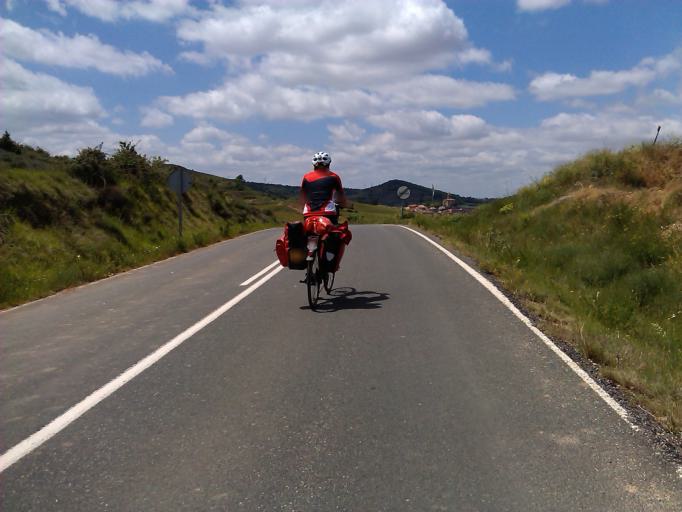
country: ES
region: La Rioja
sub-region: Provincia de La Rioja
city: Ventosa
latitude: 42.4003
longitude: -2.6133
